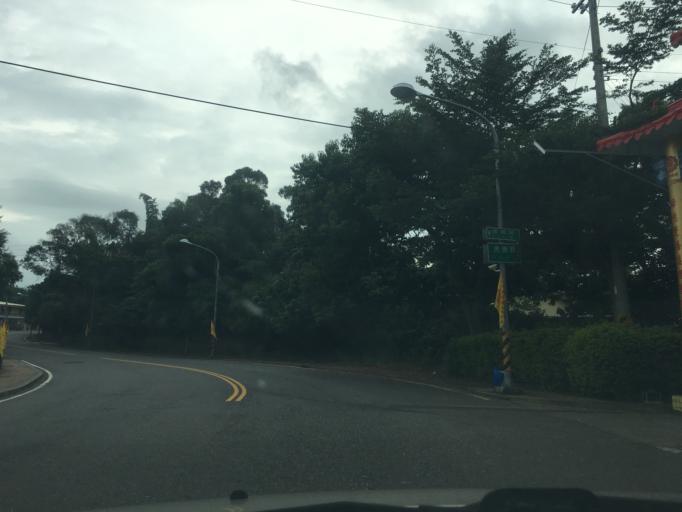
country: TW
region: Taiwan
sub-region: Changhua
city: Chang-hua
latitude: 24.0594
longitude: 120.5718
